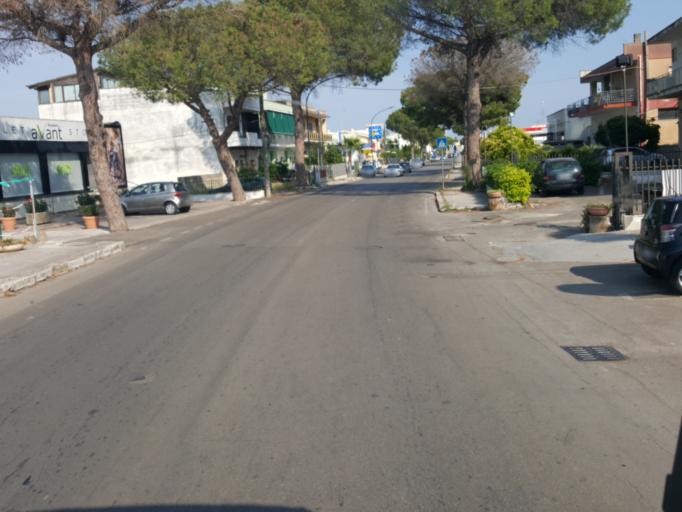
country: IT
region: Apulia
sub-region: Provincia di Lecce
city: Campi Salentina
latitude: 40.4032
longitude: 18.0176
